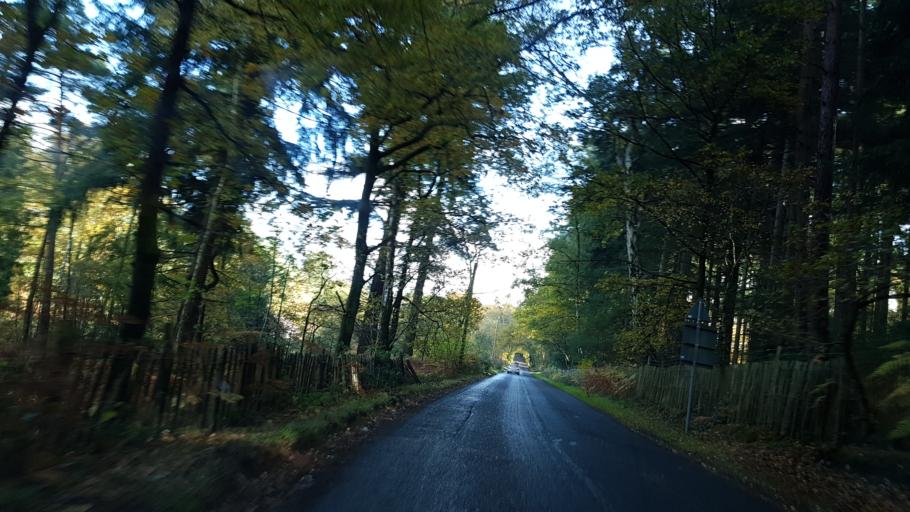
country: GB
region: England
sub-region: Surrey
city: Churt
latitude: 51.1478
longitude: -0.7520
